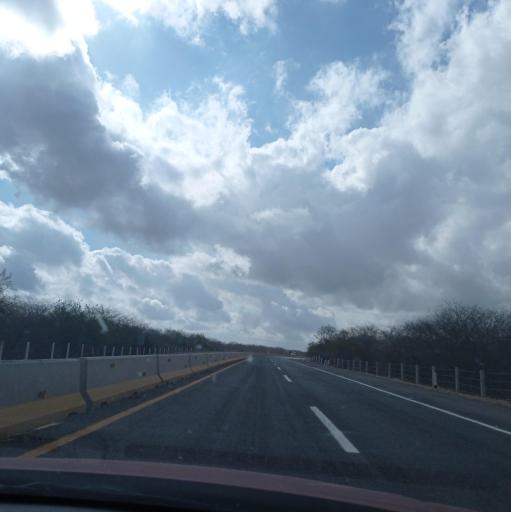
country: MX
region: Sinaloa
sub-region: Navolato
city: Juan Aldama (El Tigre)
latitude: 24.9944
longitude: -107.7760
